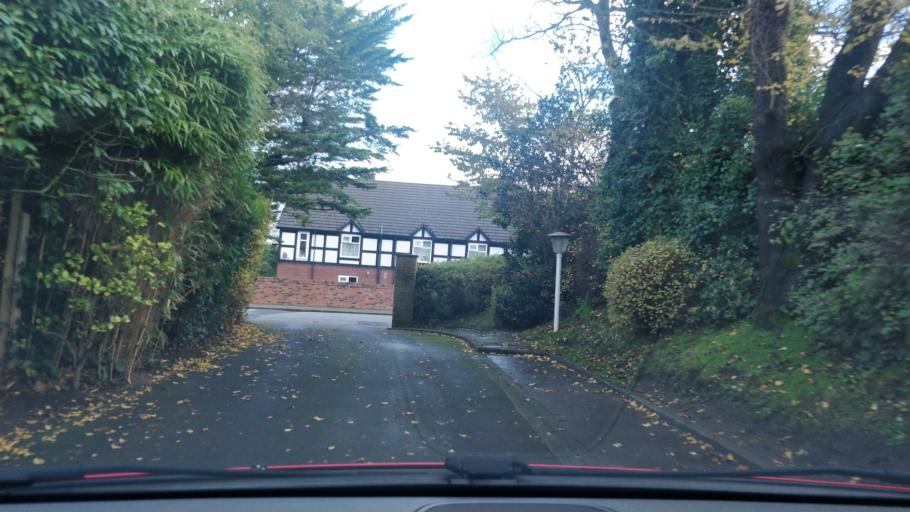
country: GB
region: England
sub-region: Sefton
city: Southport
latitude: 53.6415
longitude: -3.0199
